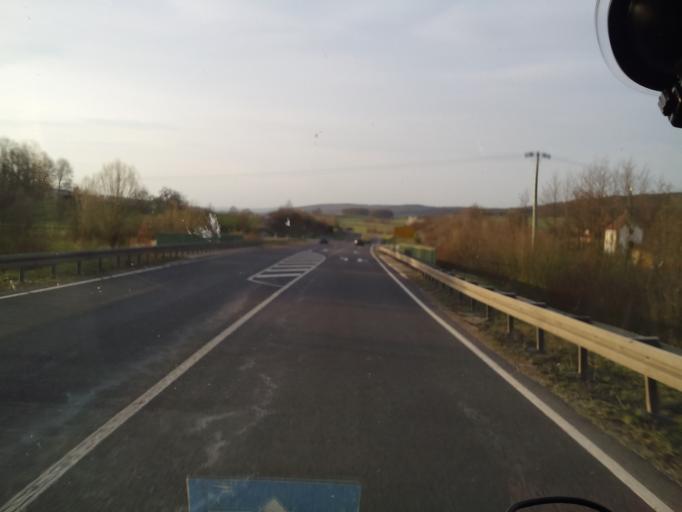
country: DE
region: Bavaria
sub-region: Upper Franconia
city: Reckendorf
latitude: 50.0322
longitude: 10.8254
